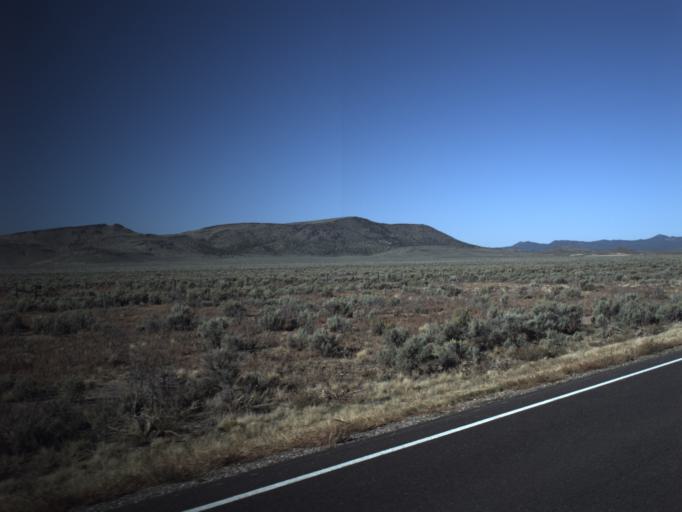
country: US
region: Utah
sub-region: Washington County
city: Enterprise
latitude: 37.7779
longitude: -113.8509
